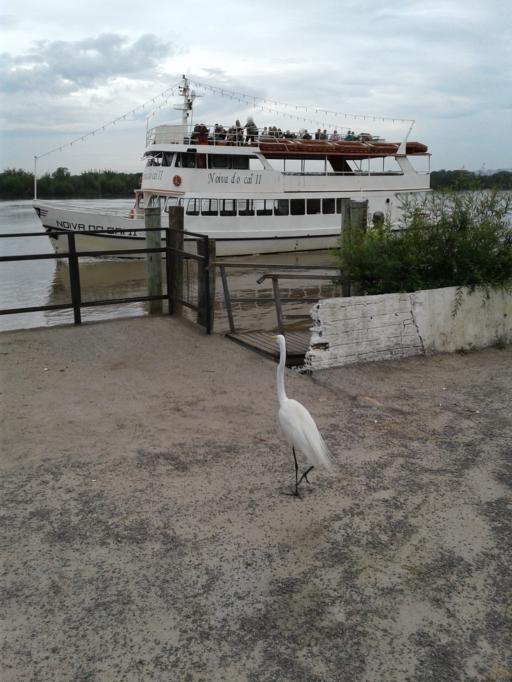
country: BR
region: Rio Grande do Sul
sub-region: Porto Alegre
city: Porto Alegre
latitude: -30.0144
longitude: -51.2588
